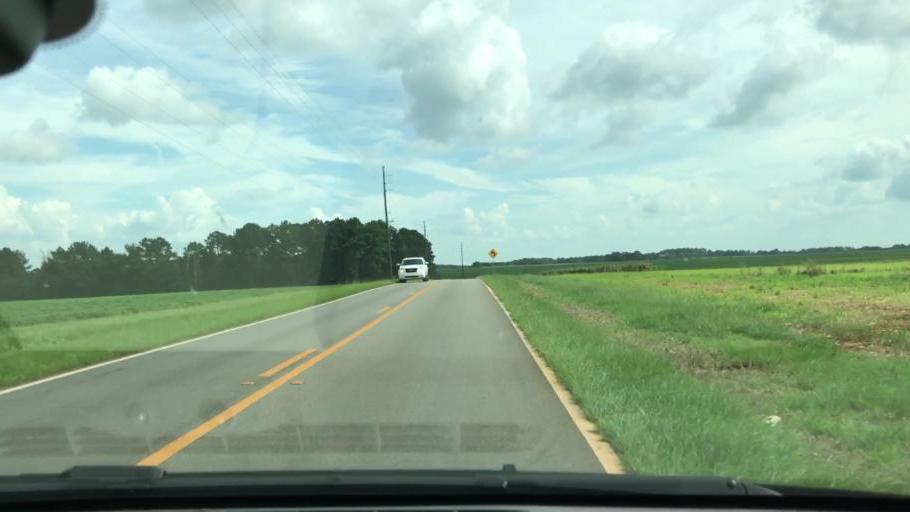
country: US
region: Georgia
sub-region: Clay County
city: Fort Gaines
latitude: 31.5357
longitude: -84.9596
